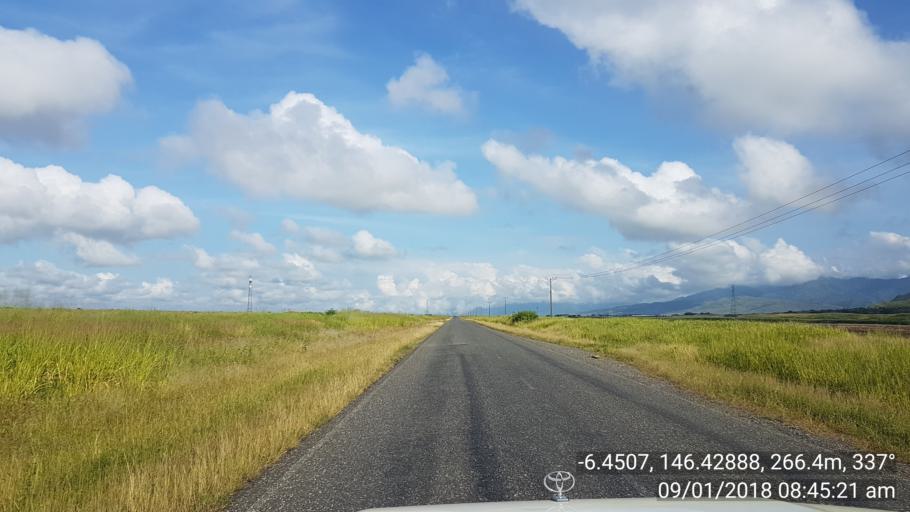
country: PG
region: Eastern Highlands
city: Kainantu
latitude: -6.4508
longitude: 146.4290
